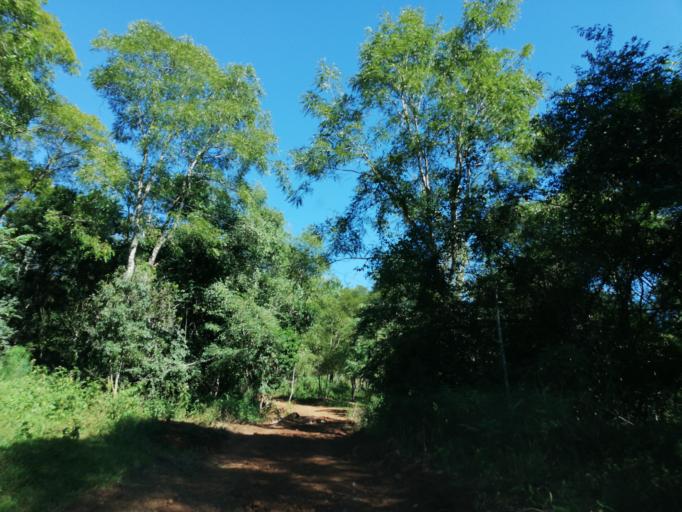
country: AR
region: Misiones
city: El Soberbio
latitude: -27.0626
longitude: -54.3738
